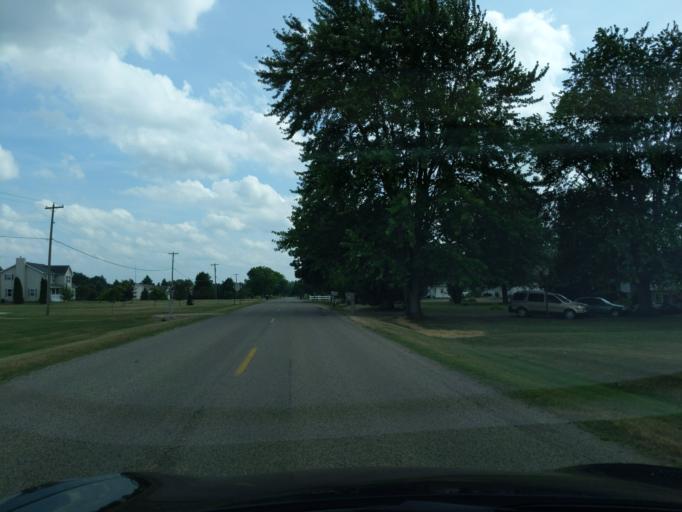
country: US
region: Michigan
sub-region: Eaton County
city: Eaton Rapids
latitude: 42.5083
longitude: -84.6308
